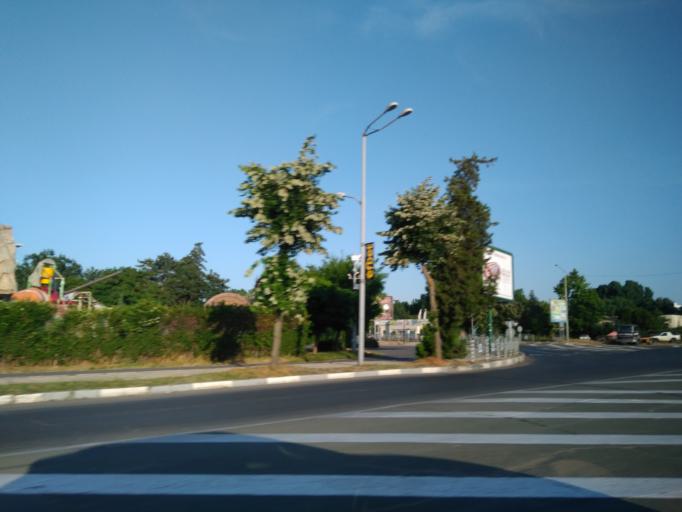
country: BG
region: Burgas
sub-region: Obshtina Nesebur
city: Nesebar
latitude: 42.6660
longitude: 27.7069
